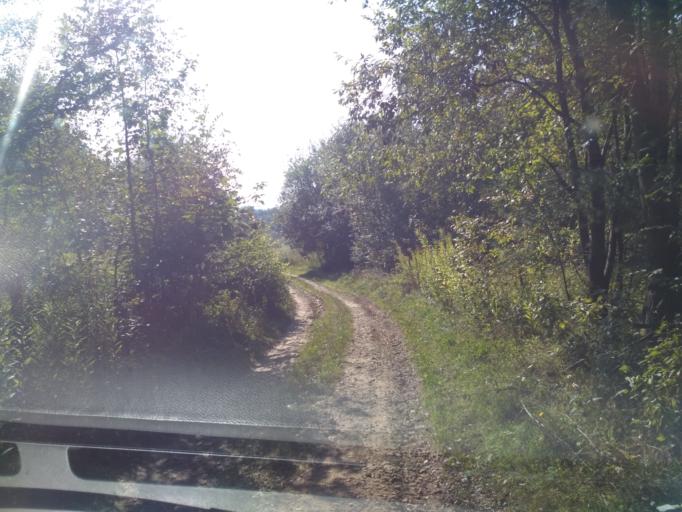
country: PL
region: Subcarpathian Voivodeship
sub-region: Powiat strzyzowski
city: Jawornik
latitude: 49.8473
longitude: 21.8578
